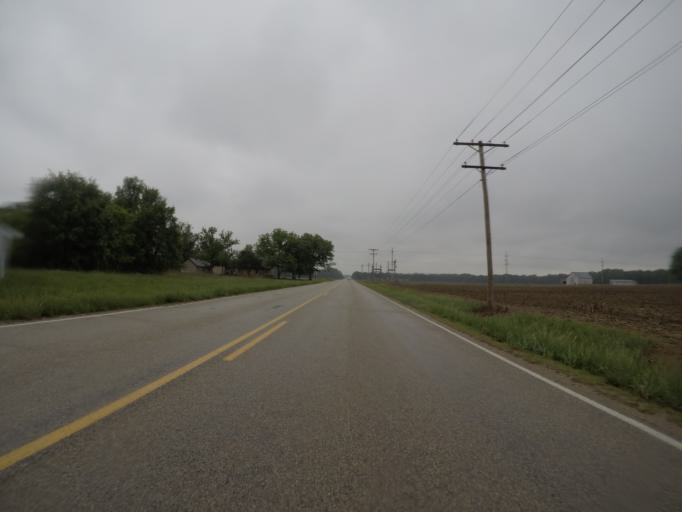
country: US
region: Kansas
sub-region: Pottawatomie County
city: Wamego
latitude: 39.2326
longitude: -96.2314
